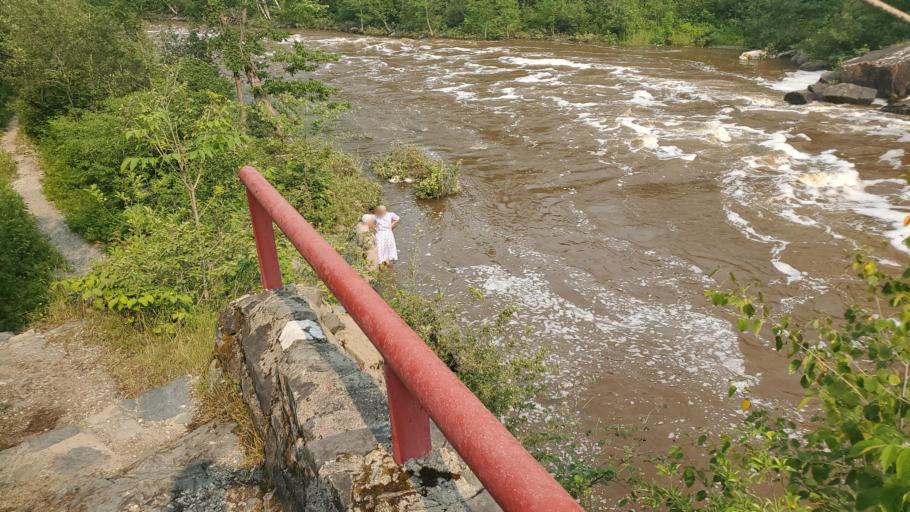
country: CA
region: Ontario
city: Englehart
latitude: 47.7959
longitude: -79.8859
